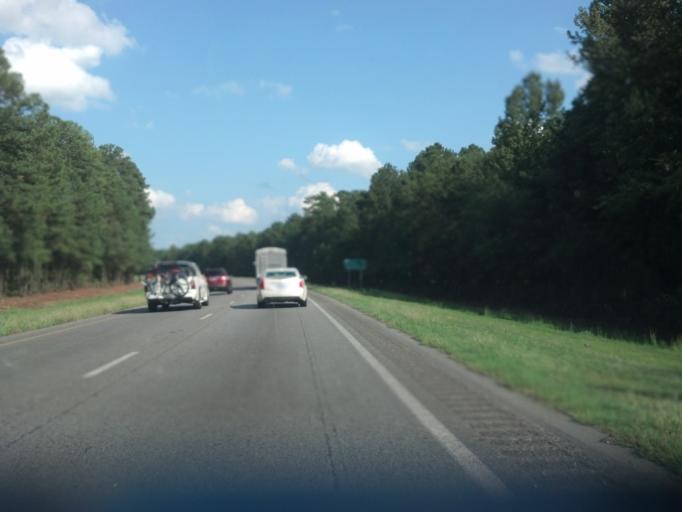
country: US
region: North Carolina
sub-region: Nash County
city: Rocky Mount
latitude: 35.9373
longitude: -77.7509
